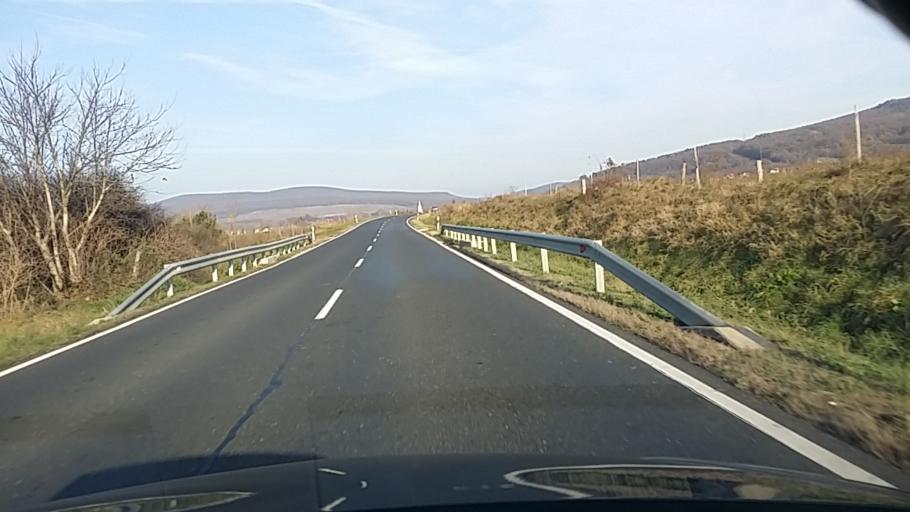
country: HU
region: Veszprem
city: Tapolca
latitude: 46.9151
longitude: 17.5389
